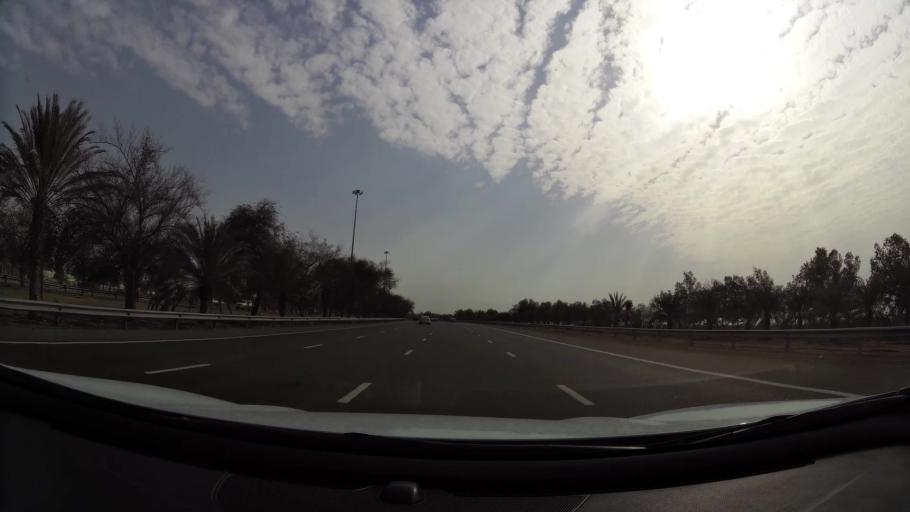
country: AE
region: Abu Dhabi
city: Abu Dhabi
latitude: 24.4884
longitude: 54.6762
